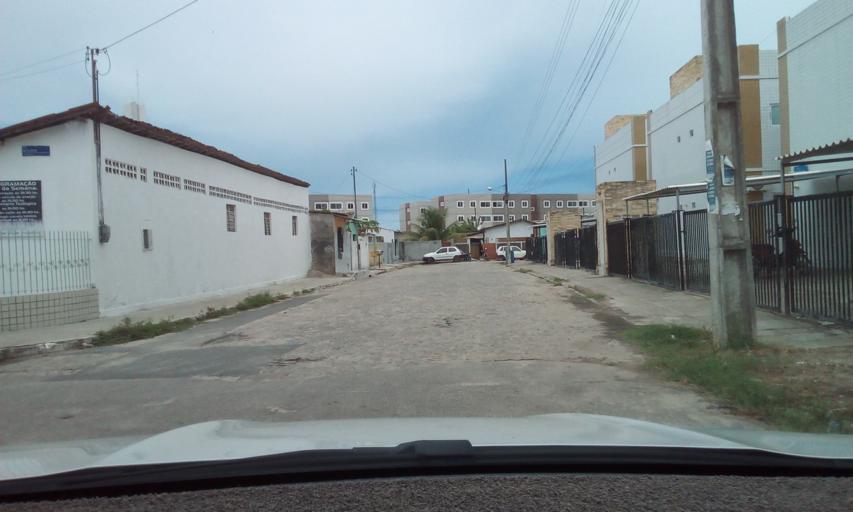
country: BR
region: Paraiba
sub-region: Conde
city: Conde
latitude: -7.2134
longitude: -34.8369
